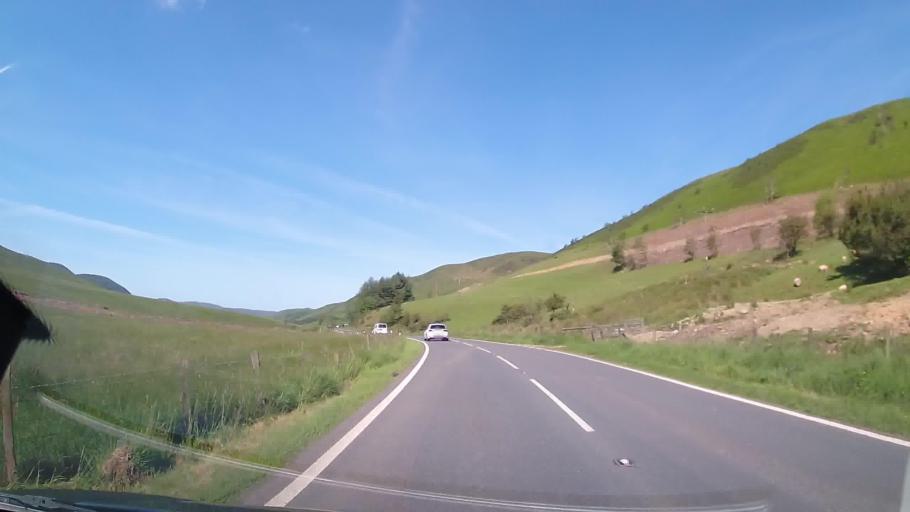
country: GB
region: Wales
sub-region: Gwynedd
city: Bala
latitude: 52.7123
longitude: -3.5782
